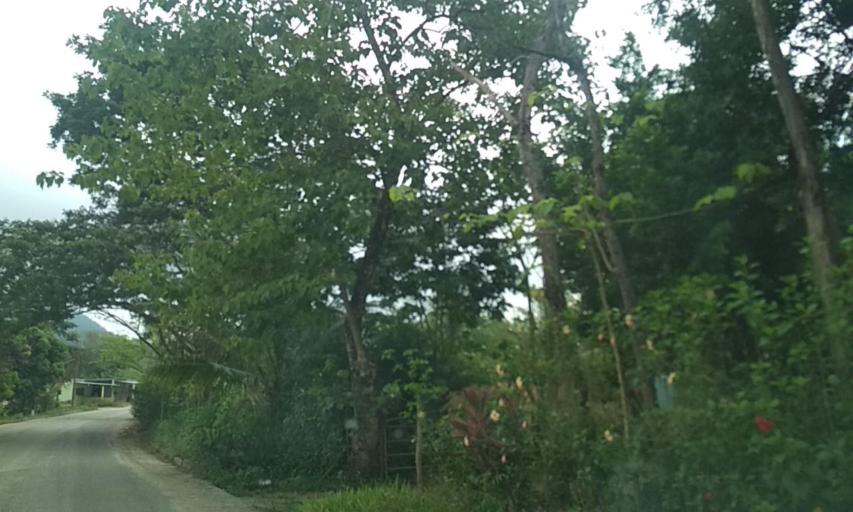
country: MX
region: Veracruz
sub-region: Uxpanapa
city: Poblado 10
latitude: 17.5082
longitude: -94.1596
